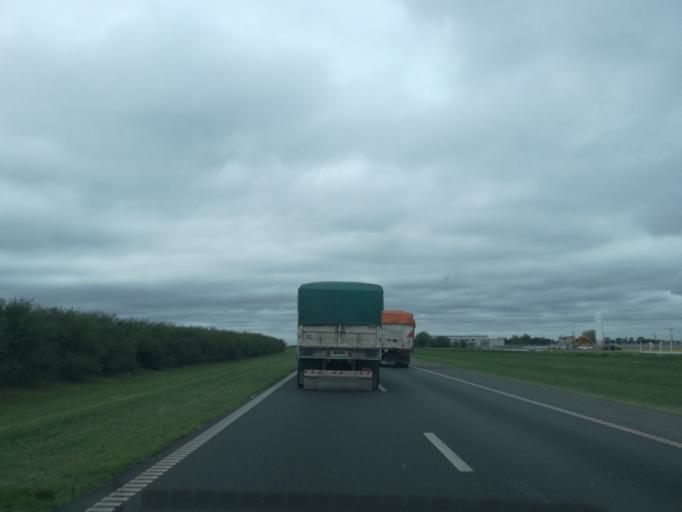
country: AR
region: Santa Fe
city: Arroyo Seco
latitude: -33.1729
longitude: -60.5244
